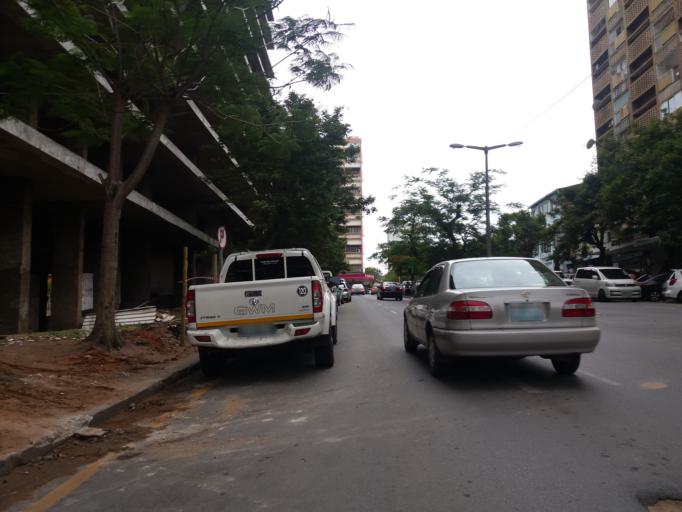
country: MZ
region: Maputo City
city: Maputo
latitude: -25.9675
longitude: 32.5749
